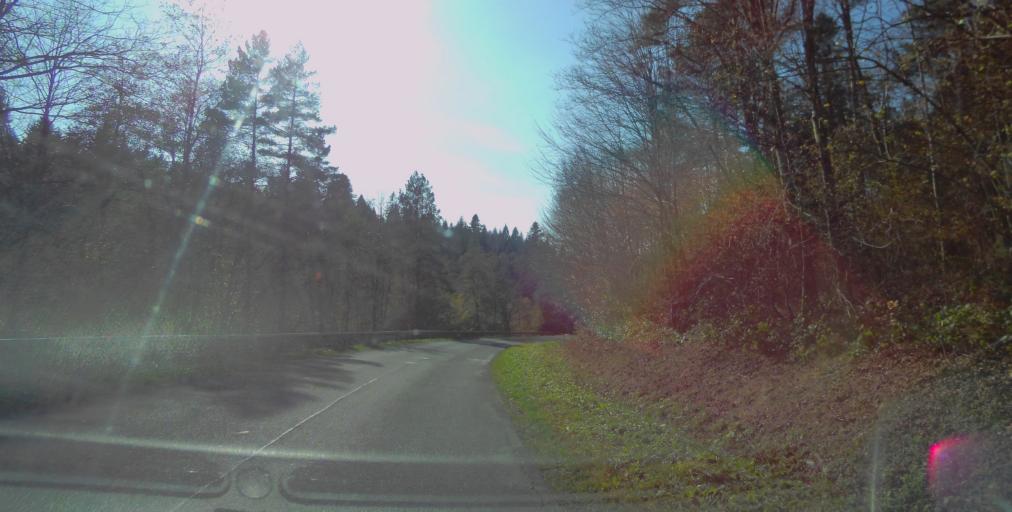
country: PL
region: Subcarpathian Voivodeship
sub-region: Powiat leski
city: Polanczyk
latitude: 49.3115
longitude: 22.4337
